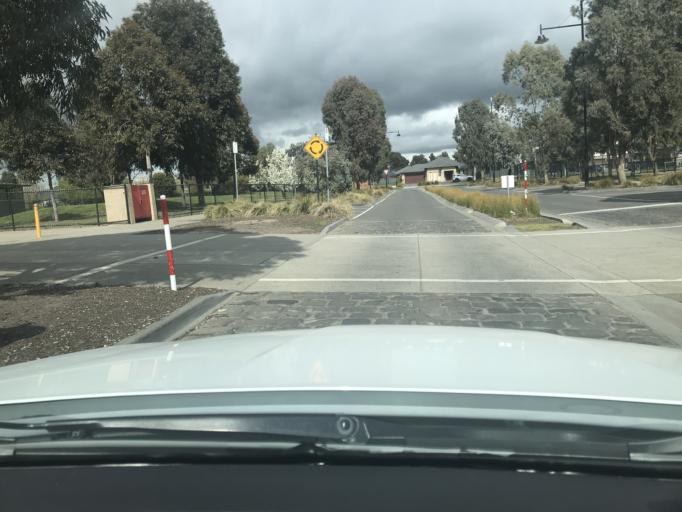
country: AU
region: Victoria
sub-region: Hume
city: Craigieburn
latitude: -37.5793
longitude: 144.9237
